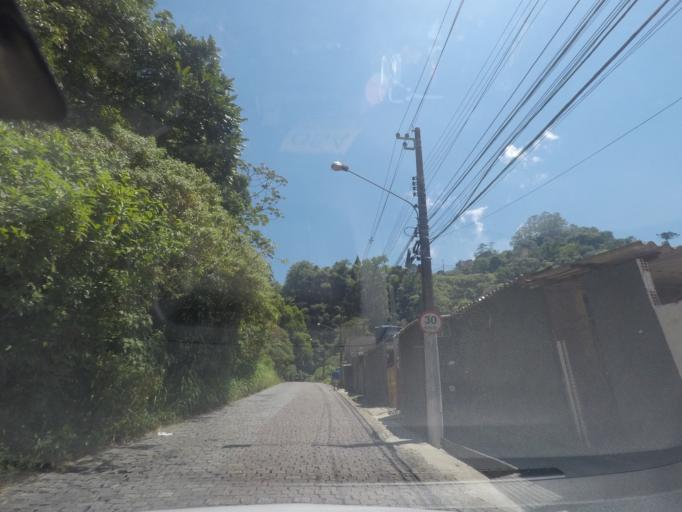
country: BR
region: Rio de Janeiro
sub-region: Petropolis
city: Petropolis
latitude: -22.5351
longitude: -43.1746
